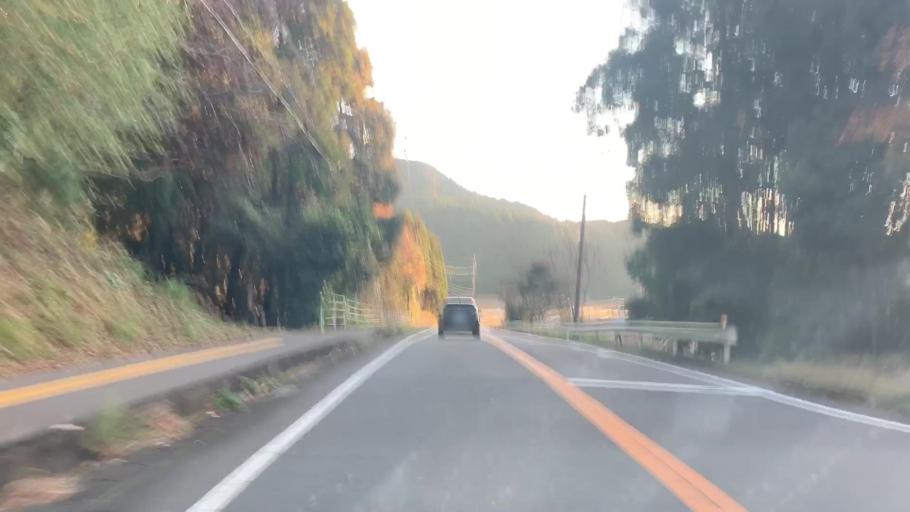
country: JP
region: Saga Prefecture
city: Karatsu
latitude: 33.3406
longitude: 129.9805
